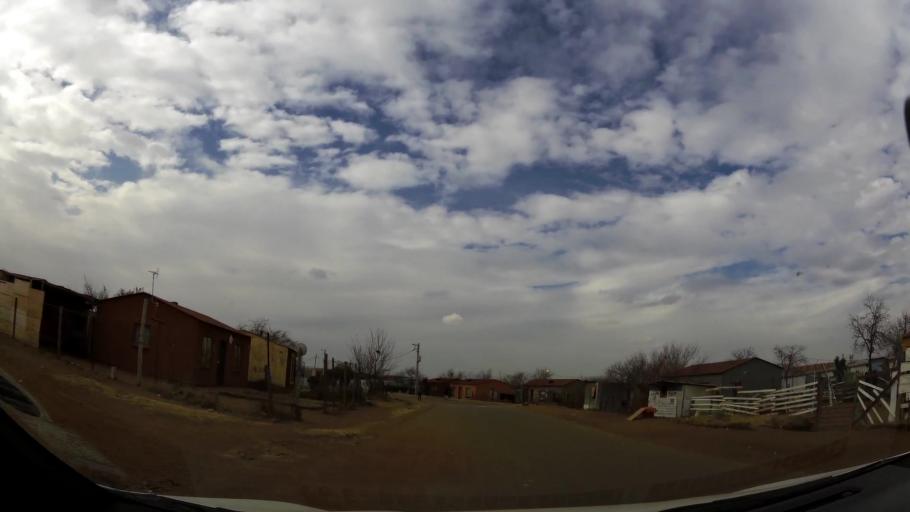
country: ZA
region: Gauteng
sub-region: Ekurhuleni Metropolitan Municipality
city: Germiston
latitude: -26.3968
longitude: 28.1550
